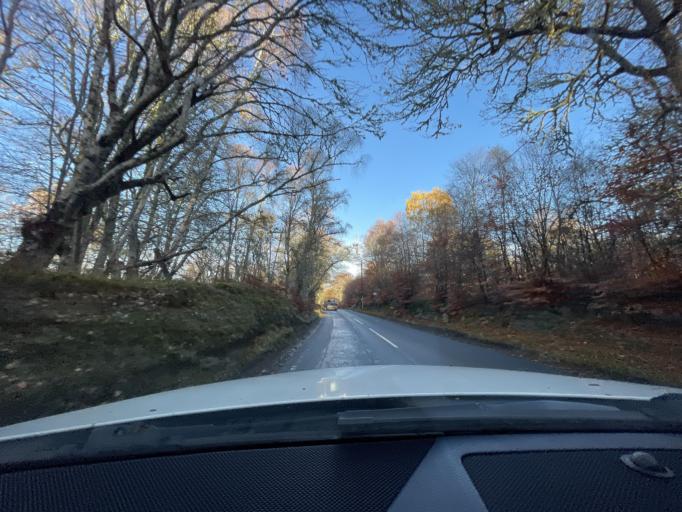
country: GB
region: Scotland
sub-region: Highland
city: Inverness
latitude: 57.4391
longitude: -4.2647
